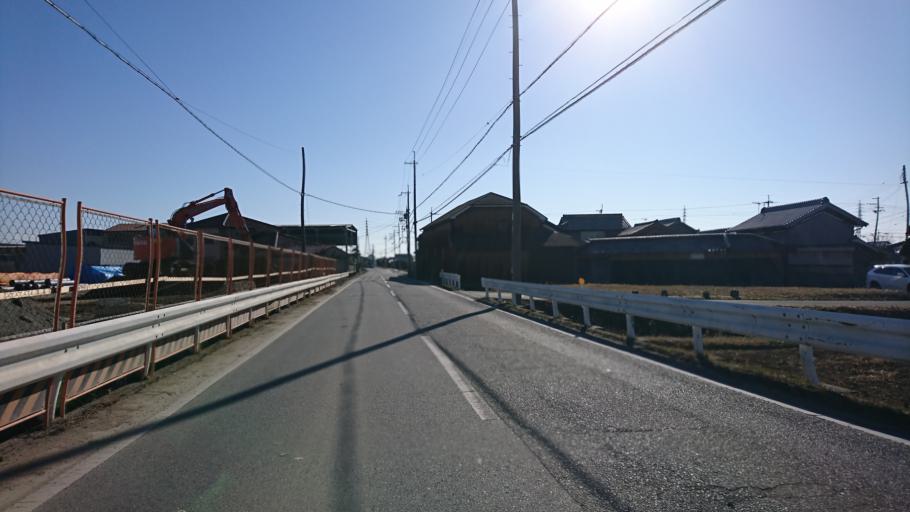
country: JP
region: Hyogo
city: Miki
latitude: 34.7480
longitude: 134.9320
